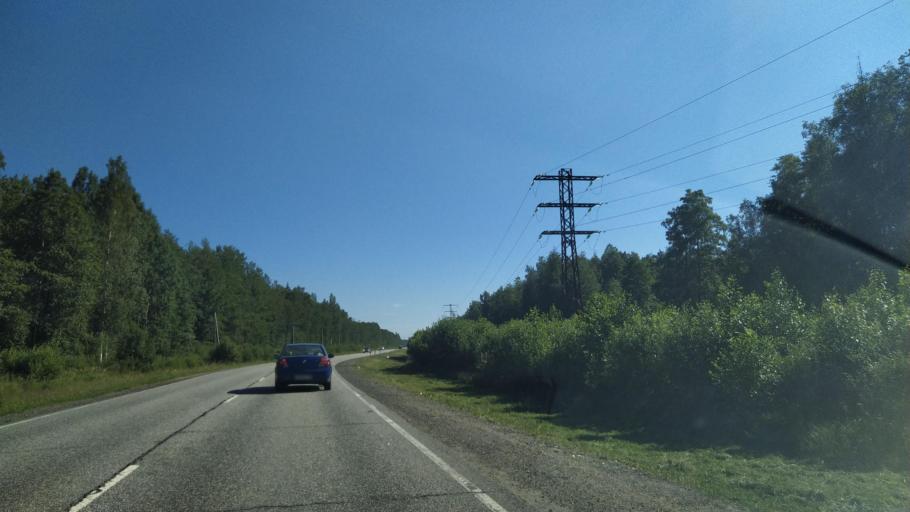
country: RU
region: Leningrad
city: Imeni Morozova
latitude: 60.0432
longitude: 31.0356
